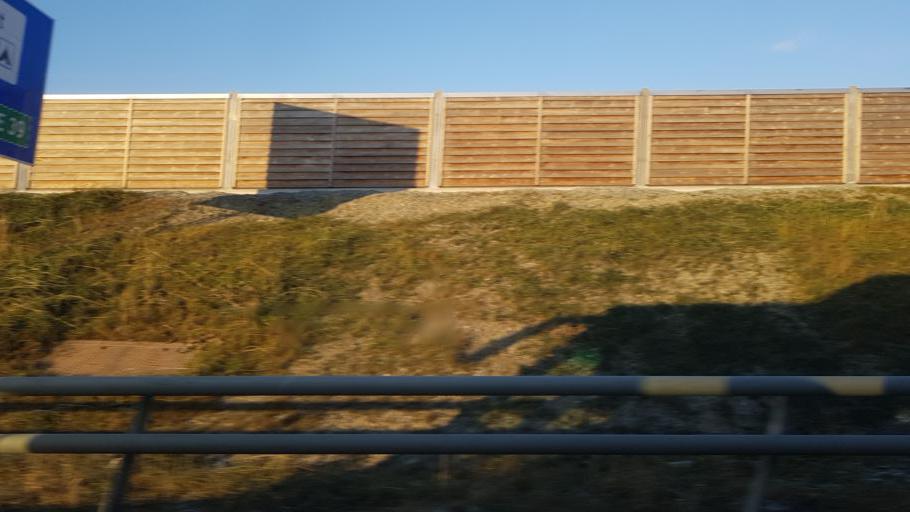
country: NO
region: Sor-Trondelag
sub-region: Melhus
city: Melhus
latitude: 63.3262
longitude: 10.3284
